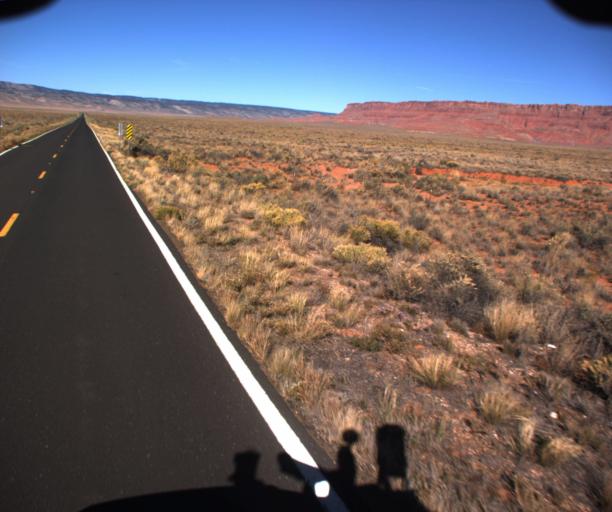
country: US
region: Arizona
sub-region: Coconino County
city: Page
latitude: 36.6993
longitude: -111.9229
